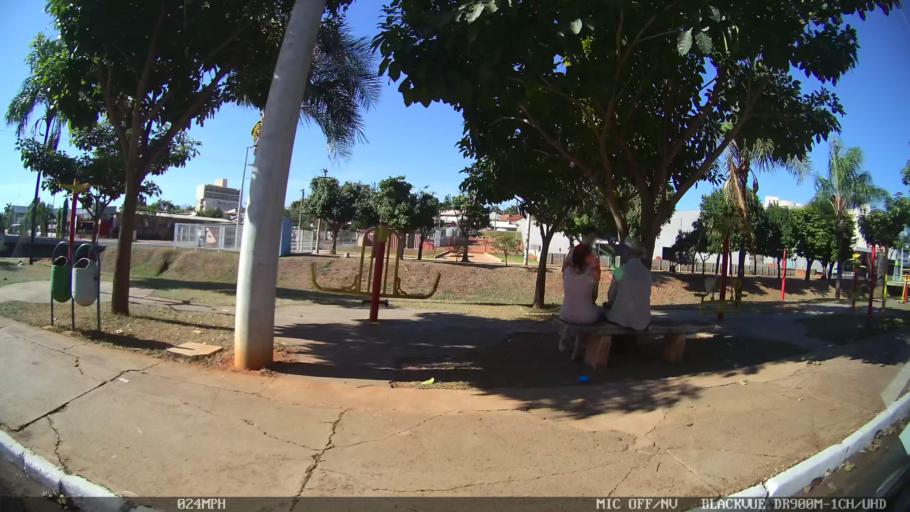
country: BR
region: Sao Paulo
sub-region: Olimpia
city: Olimpia
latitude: -20.7352
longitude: -48.9118
